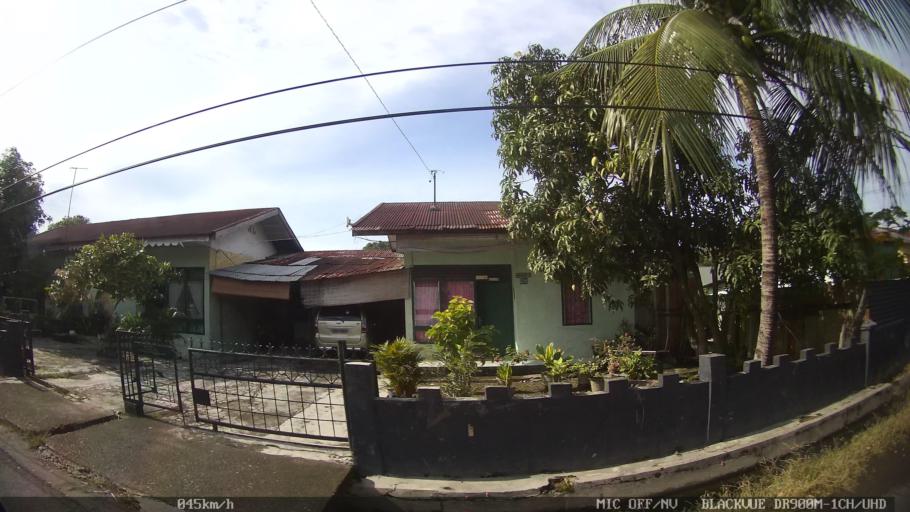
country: ID
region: North Sumatra
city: Medan
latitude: 3.6117
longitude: 98.6486
